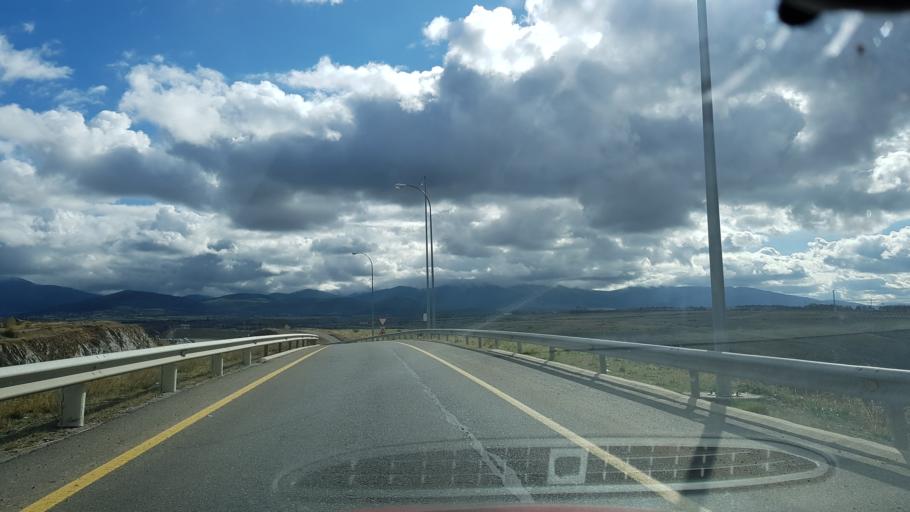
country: ES
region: Castille and Leon
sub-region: Provincia de Segovia
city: San Cristobal de Segovia
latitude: 40.9522
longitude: -4.0911
